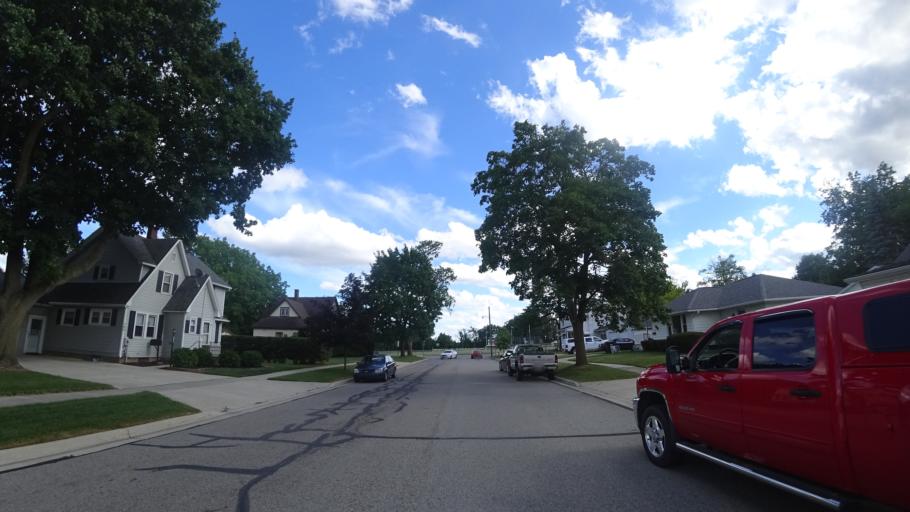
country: US
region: Michigan
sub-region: Ionia County
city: Portland
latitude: 42.8723
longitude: -84.9103
